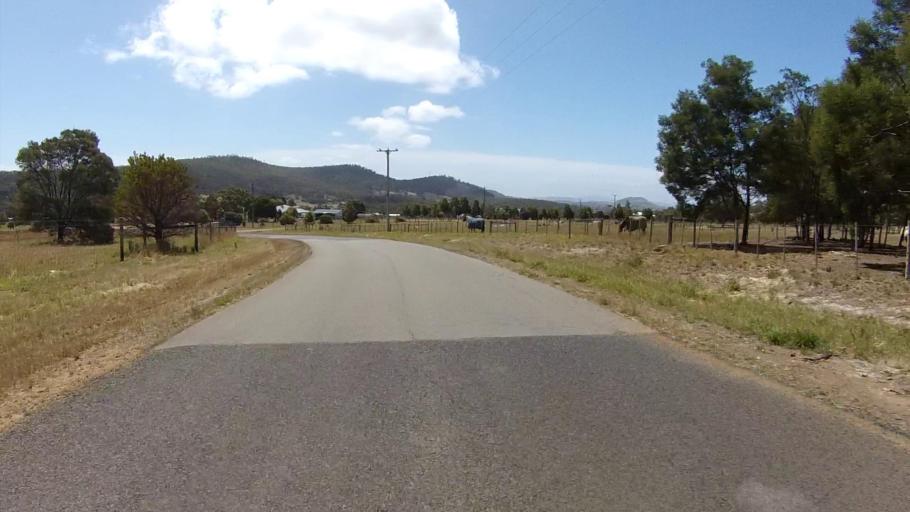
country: AU
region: Tasmania
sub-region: Clarence
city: Sandford
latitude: -42.9579
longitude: 147.4828
